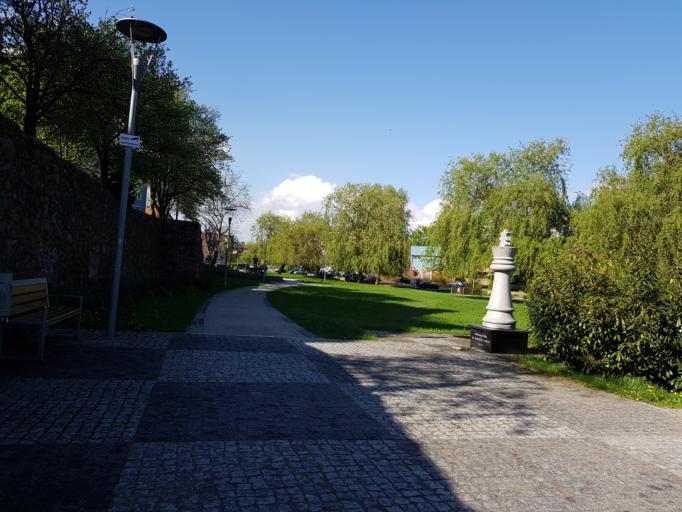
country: PL
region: West Pomeranian Voivodeship
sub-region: Powiat mysliborski
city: Barlinek
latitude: 52.9924
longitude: 15.2197
